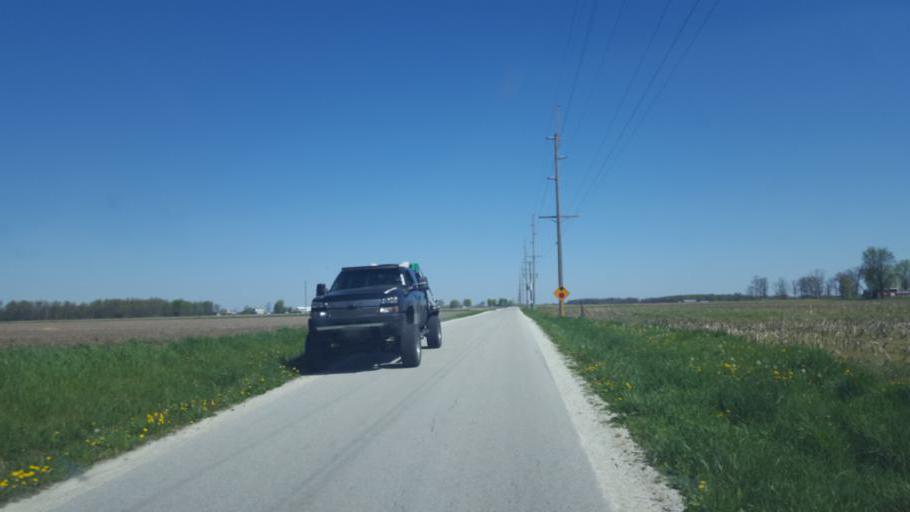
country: US
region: Ohio
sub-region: Sandusky County
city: Ballville
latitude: 41.2709
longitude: -83.1879
